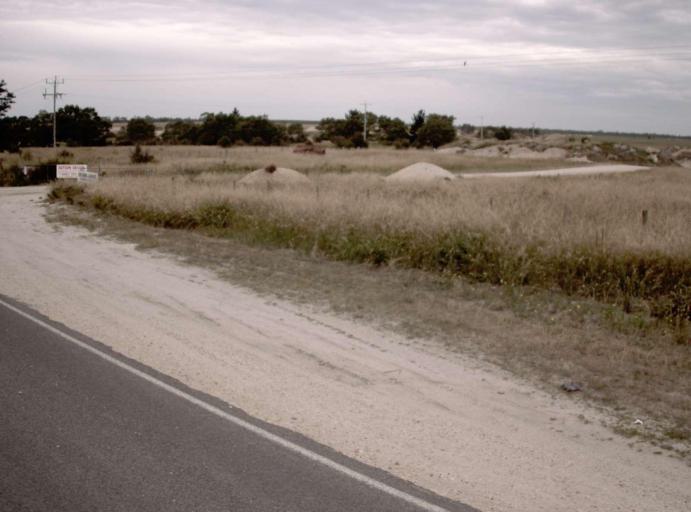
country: AU
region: Victoria
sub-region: Wellington
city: Sale
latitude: -38.1856
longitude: 147.2722
